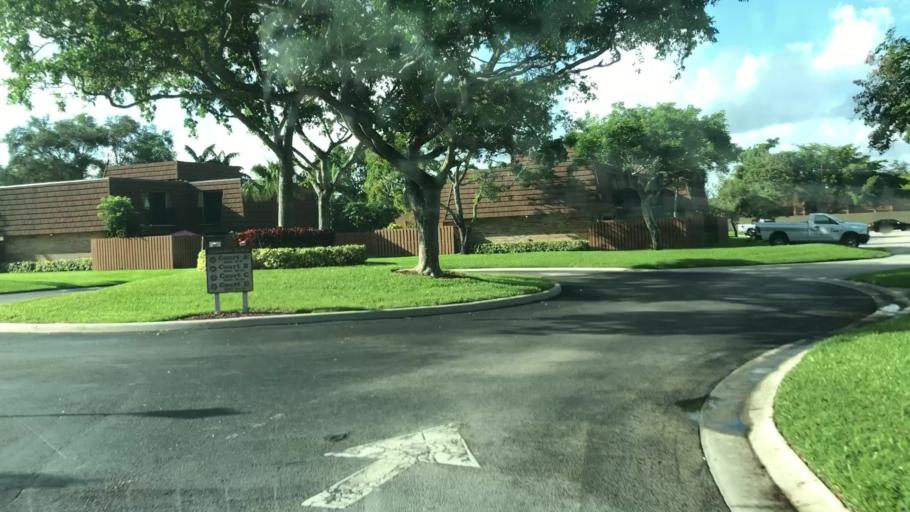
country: US
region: Florida
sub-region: Broward County
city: Sunshine Ranches
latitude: 26.0315
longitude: -80.3097
